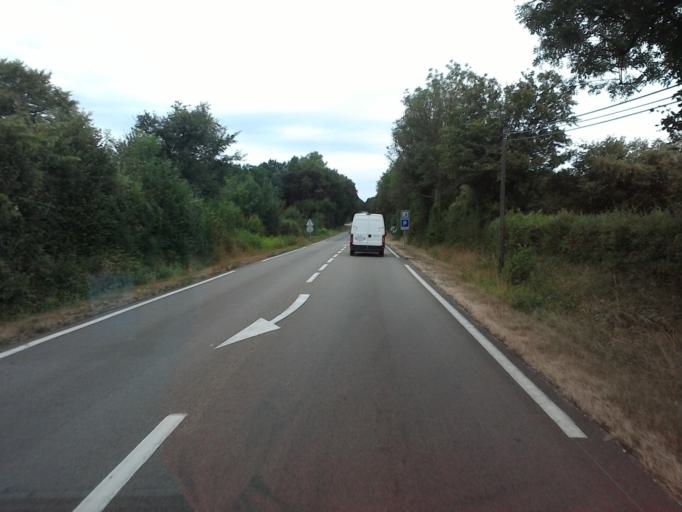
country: FR
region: Rhone-Alpes
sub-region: Departement de l'Isere
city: Bouvesse-Quirieu
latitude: 45.7666
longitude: 5.4021
